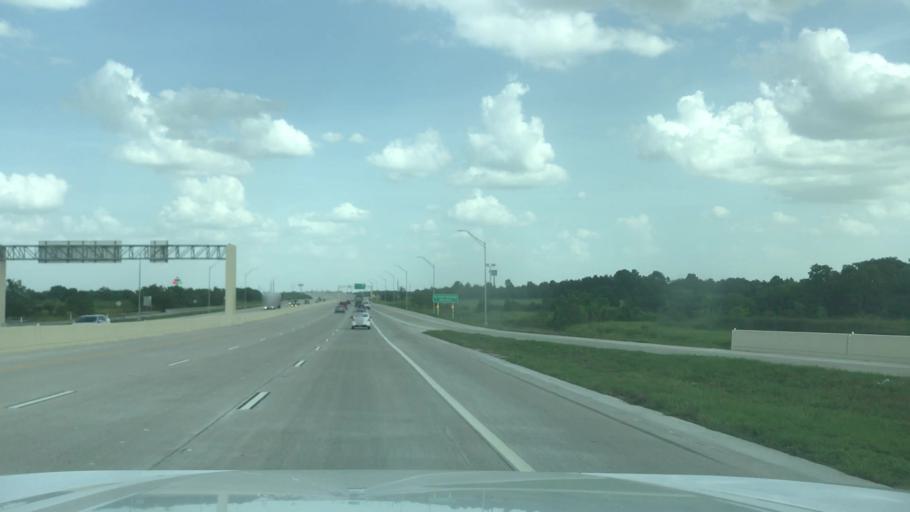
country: US
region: Texas
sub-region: Waller County
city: Waller
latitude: 30.0675
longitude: -95.9184
